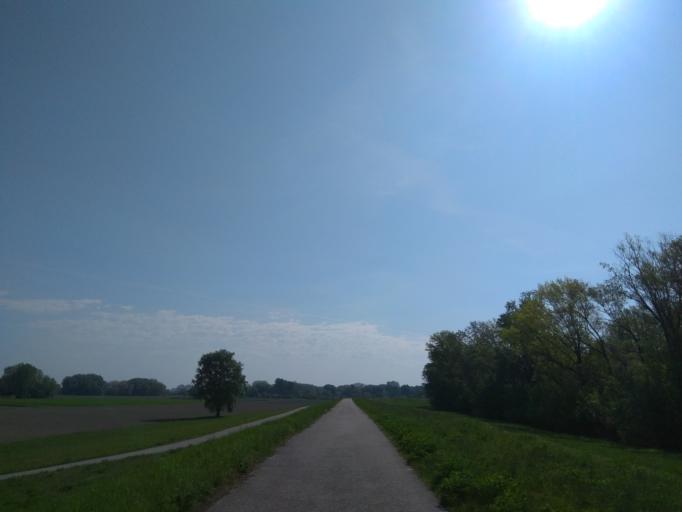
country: SK
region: Trnavsky
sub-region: Okres Dunajska Streda
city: Velky Meder
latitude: 47.7960
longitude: 17.6764
